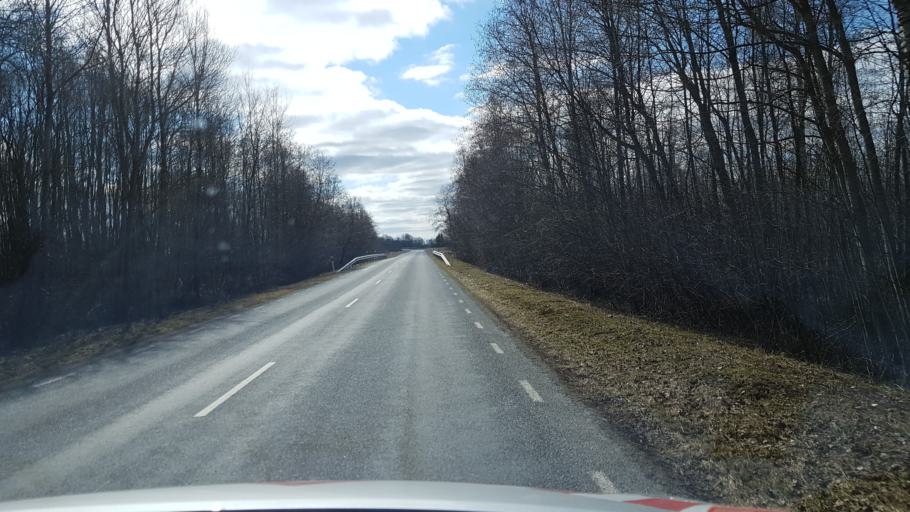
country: EE
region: Laeaene-Virumaa
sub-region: Tapa vald
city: Tapa
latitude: 59.2613
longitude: 25.8456
